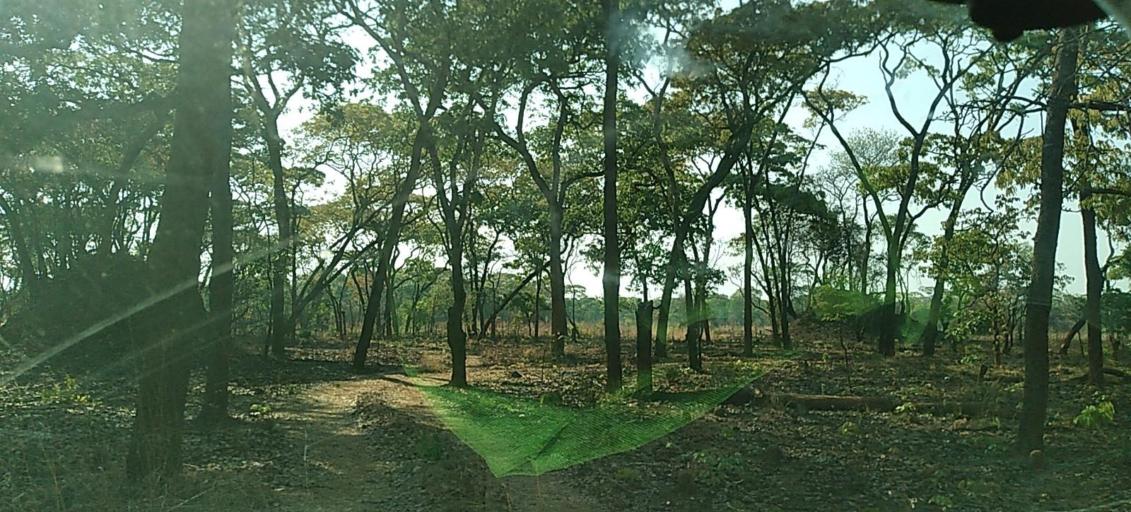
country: ZM
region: North-Western
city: Kalengwa
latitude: -13.2381
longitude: 25.0533
